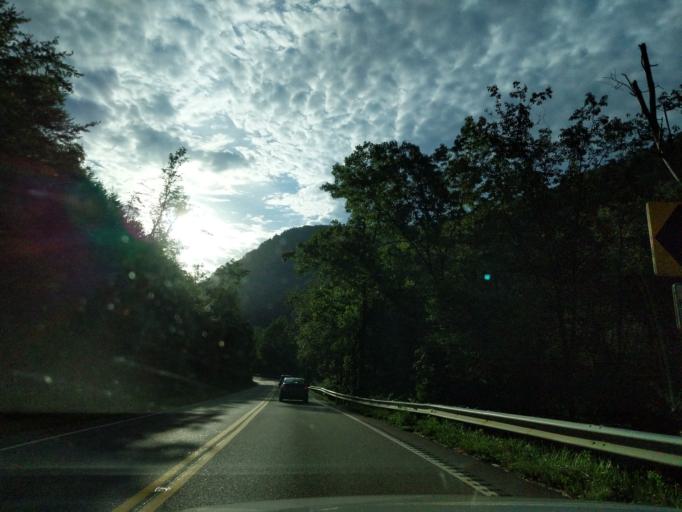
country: US
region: Tennessee
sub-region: Polk County
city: Benton
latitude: 35.0817
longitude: -84.5286
